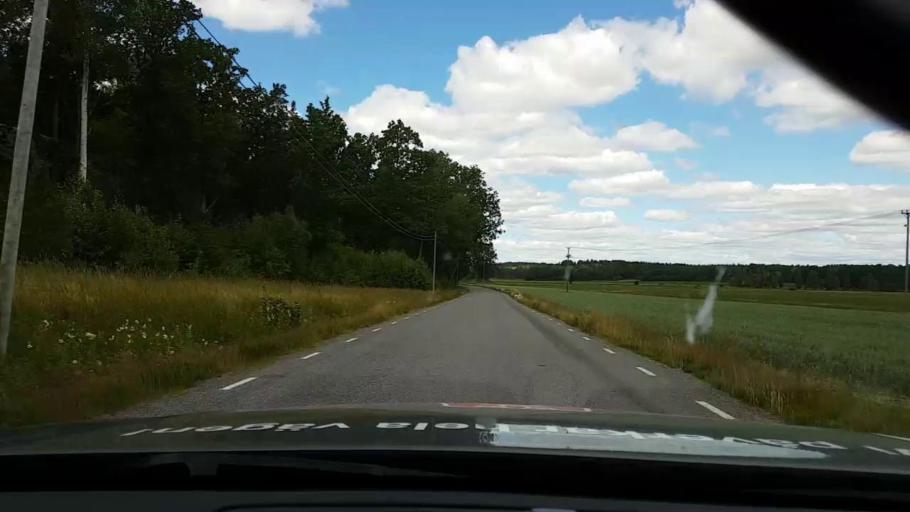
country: SE
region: Kalmar
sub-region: Vasterviks Kommun
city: Forserum
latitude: 57.9875
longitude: 16.6060
